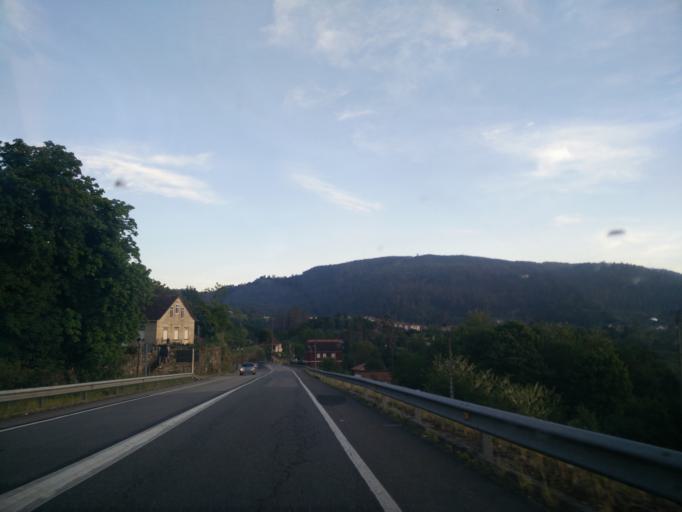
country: ES
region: Galicia
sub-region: Provincia de Pontevedra
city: Mondariz
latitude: 42.2310
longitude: -8.4591
